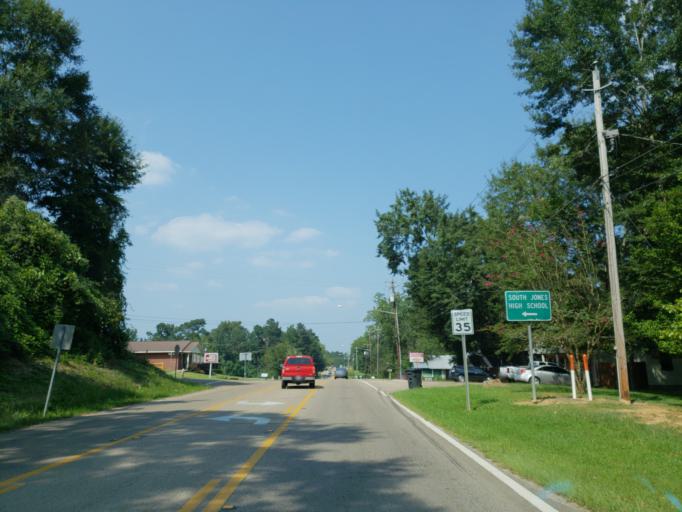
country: US
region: Mississippi
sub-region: Jones County
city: Ellisville
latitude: 31.6093
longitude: -89.1942
